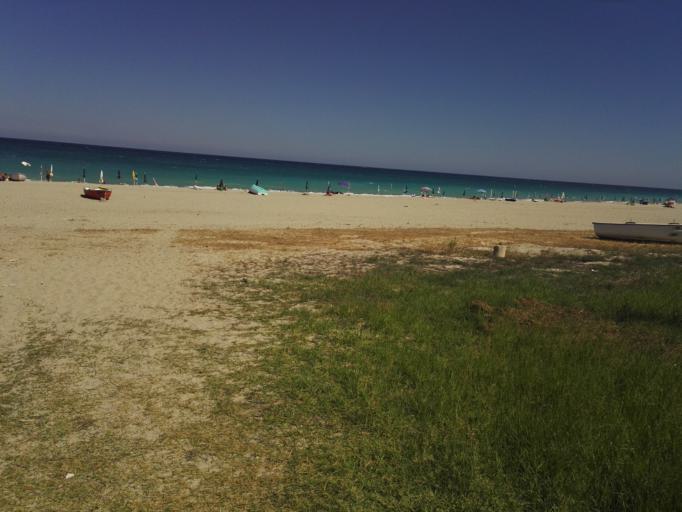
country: IT
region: Calabria
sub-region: Provincia di Catanzaro
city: Santa Caterina dello Ionio Marina
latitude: 38.5293
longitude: 16.5720
